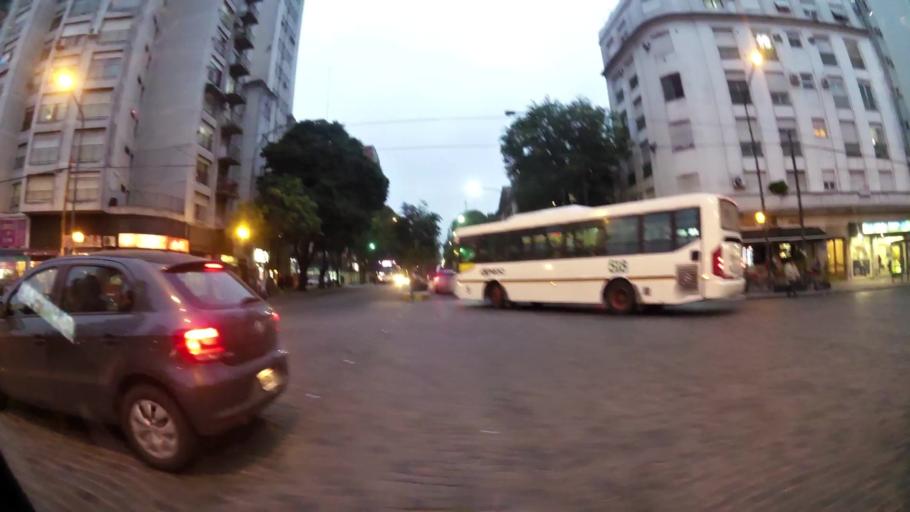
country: AR
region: Buenos Aires
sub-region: Partido de La Plata
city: La Plata
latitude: -34.9112
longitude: -57.9547
